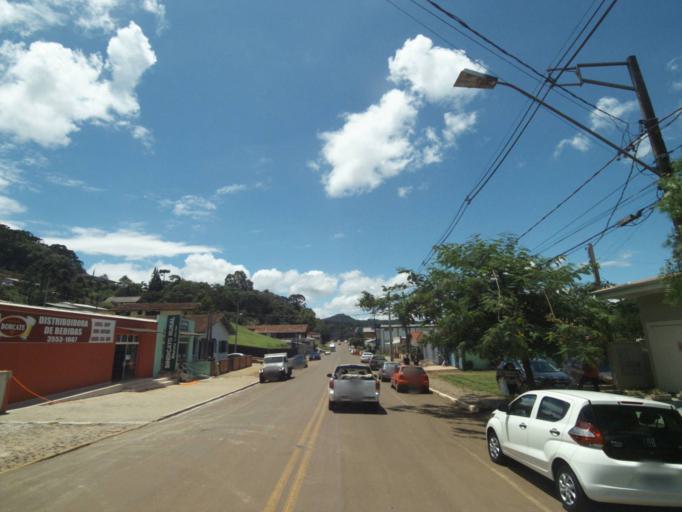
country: BR
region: Parana
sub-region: Uniao Da Vitoria
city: Uniao da Vitoria
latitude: -26.1638
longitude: -51.5549
